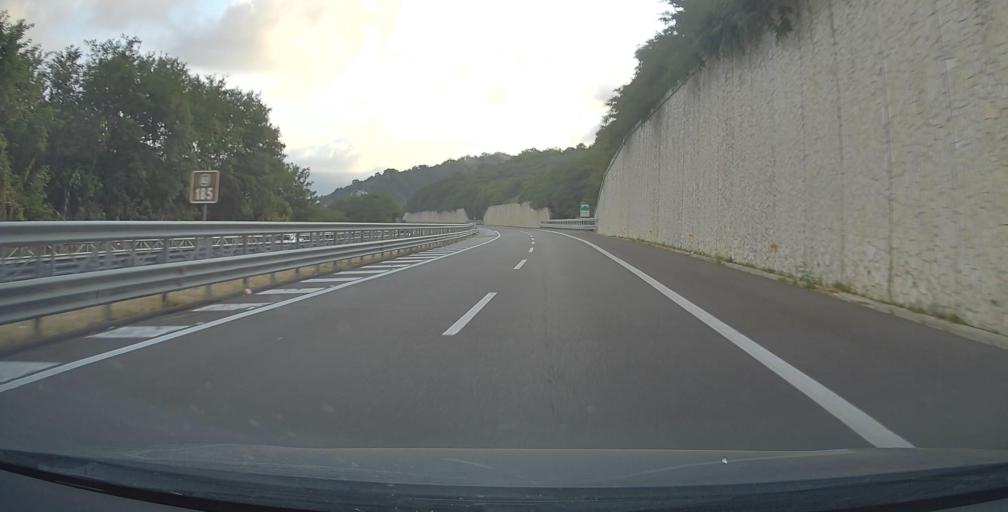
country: IT
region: Calabria
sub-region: Provincia di Catanzaro
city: Nocera Scalo
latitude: 39.0305
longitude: 16.1317
